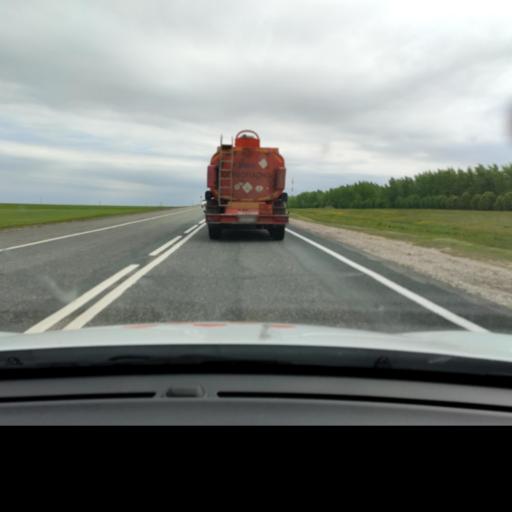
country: RU
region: Tatarstan
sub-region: Alekseyevskiy Rayon
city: Alekseyevskoye
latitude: 55.3826
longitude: 49.9129
